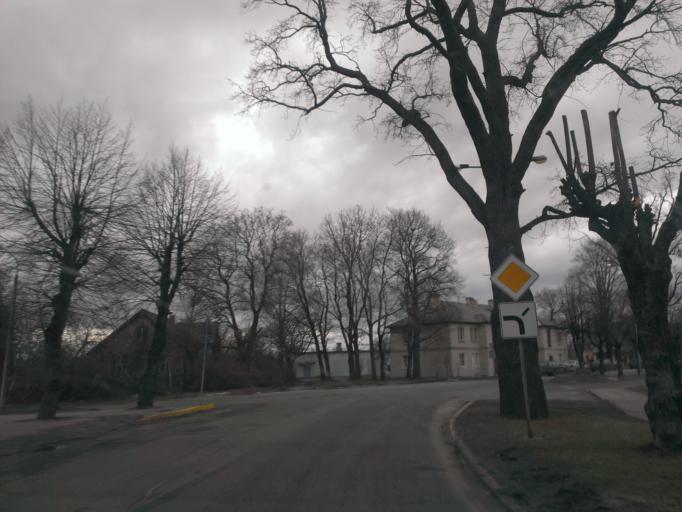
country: LV
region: Salaspils
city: Salaspils
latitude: 56.8584
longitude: 24.3496
